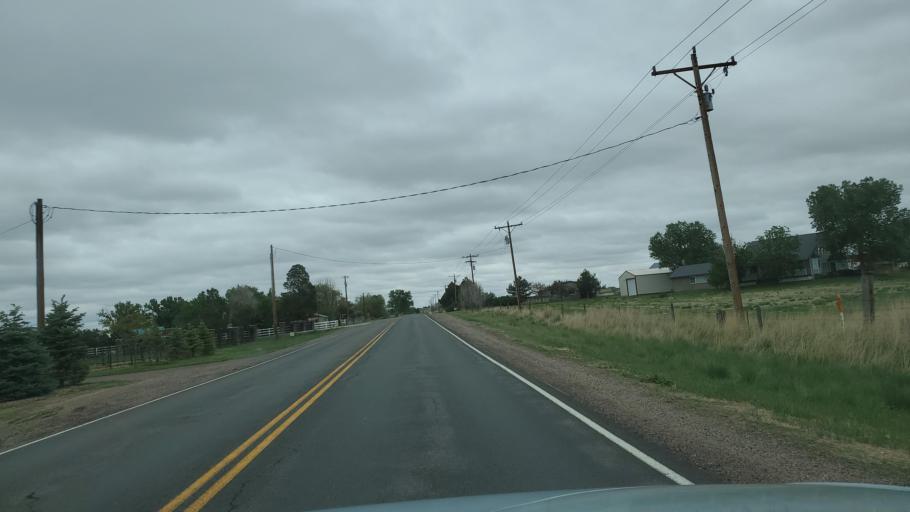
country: US
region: Colorado
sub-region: Weld County
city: Lochbuie
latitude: 39.9725
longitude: -104.7115
